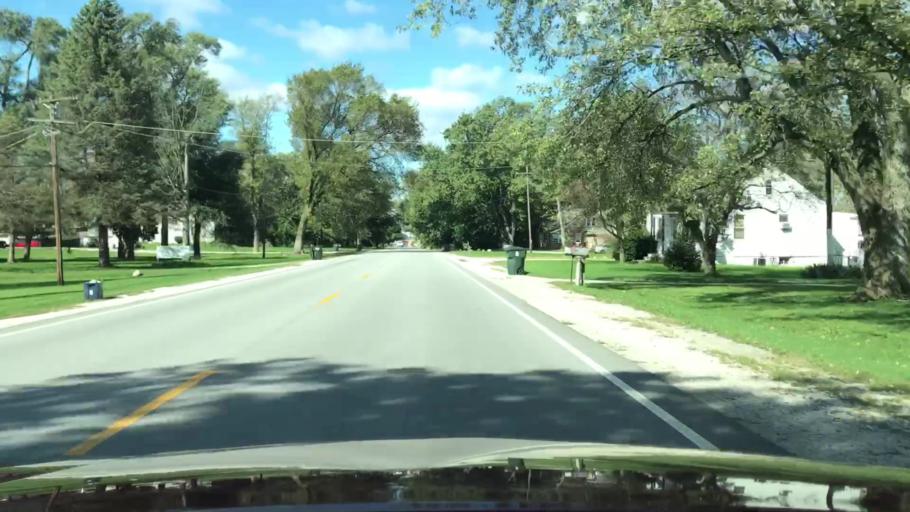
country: US
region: Illinois
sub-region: Cook County
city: Lynwood
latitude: 41.5205
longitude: -87.5508
